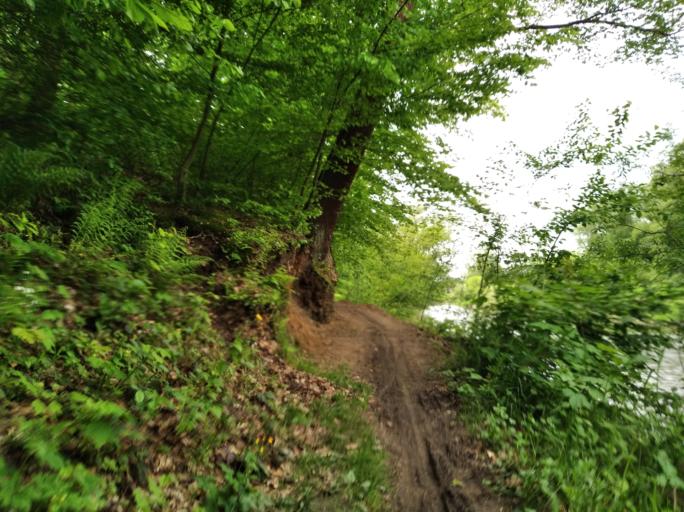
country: PL
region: Subcarpathian Voivodeship
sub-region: Powiat strzyzowski
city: Czudec
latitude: 49.9378
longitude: 21.8335
